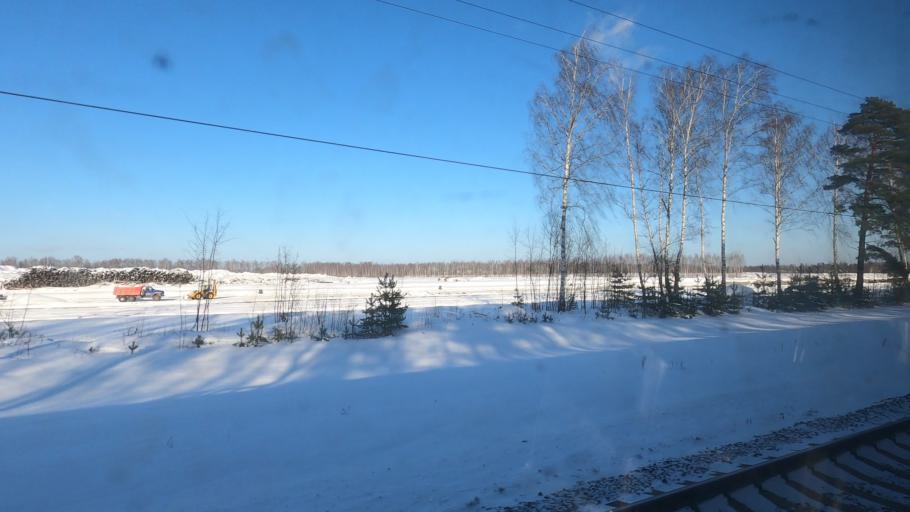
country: RU
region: Moskovskaya
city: Imeni Vorovskogo
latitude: 55.7227
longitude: 38.2670
